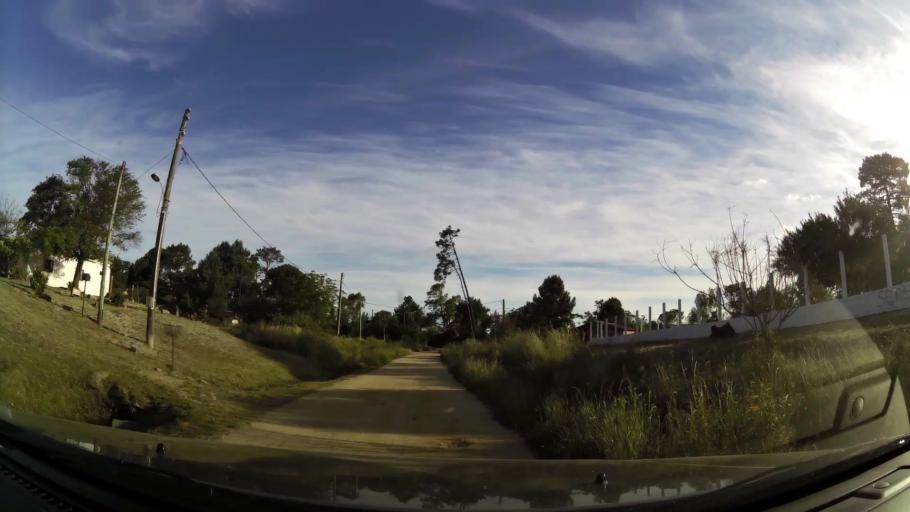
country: UY
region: Canelones
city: Empalme Olmos
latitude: -34.7709
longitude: -55.8598
